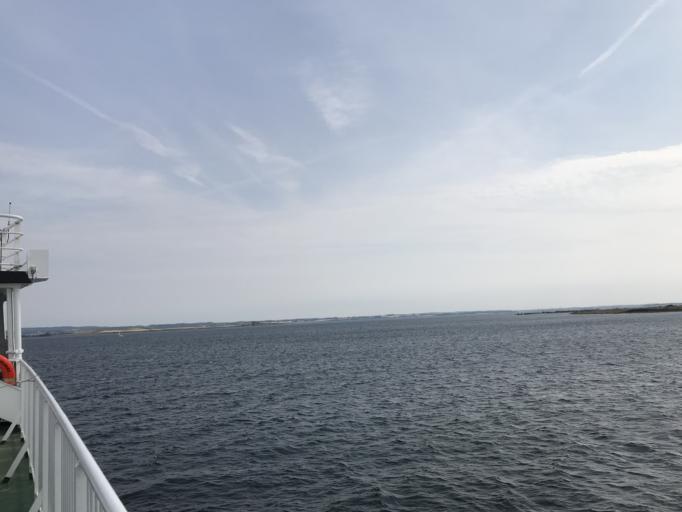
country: DK
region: South Denmark
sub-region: Faaborg-Midtfyn Kommune
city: Faaborg
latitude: 55.0368
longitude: 10.2271
